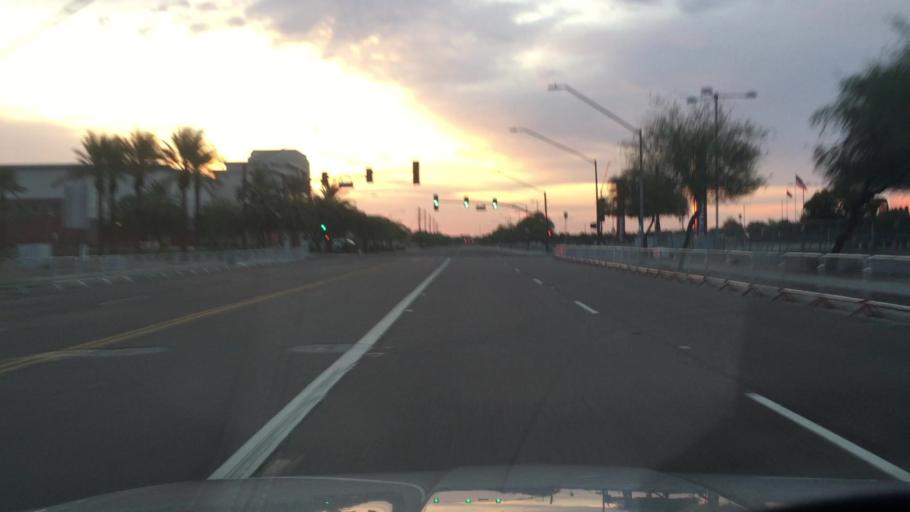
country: US
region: Arizona
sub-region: Maricopa County
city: Peoria
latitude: 33.5301
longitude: -112.2657
